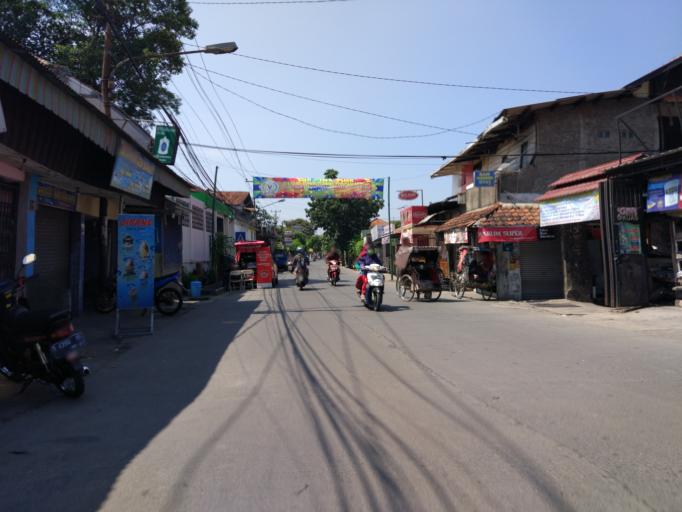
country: ID
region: West Java
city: Bandung
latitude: -6.9226
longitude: 107.6517
